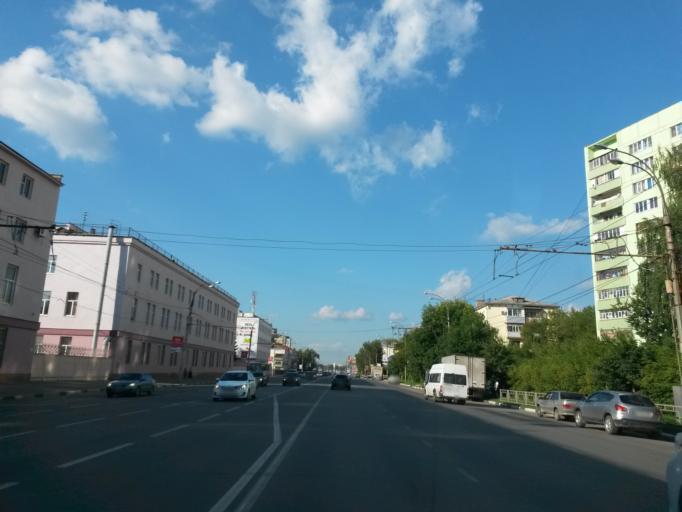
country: RU
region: Ivanovo
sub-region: Gorod Ivanovo
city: Ivanovo
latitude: 56.9762
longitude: 40.9756
